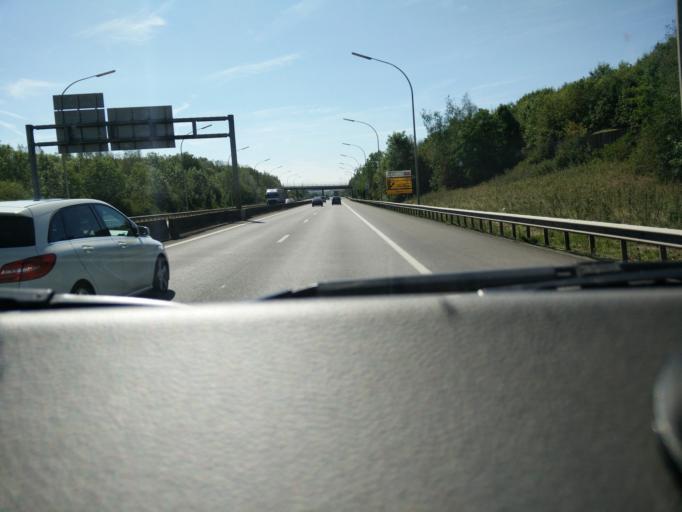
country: LU
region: Luxembourg
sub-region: Canton de Luxembourg
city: Strassen
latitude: 49.6150
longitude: 6.0827
